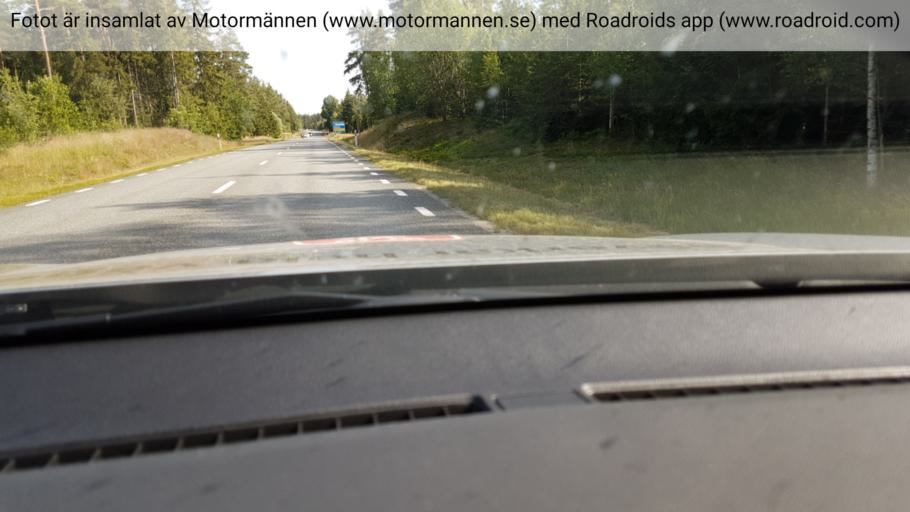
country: SE
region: Joenkoeping
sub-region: Vetlanda Kommun
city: Ekenassjon
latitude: 57.5618
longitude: 14.9781
